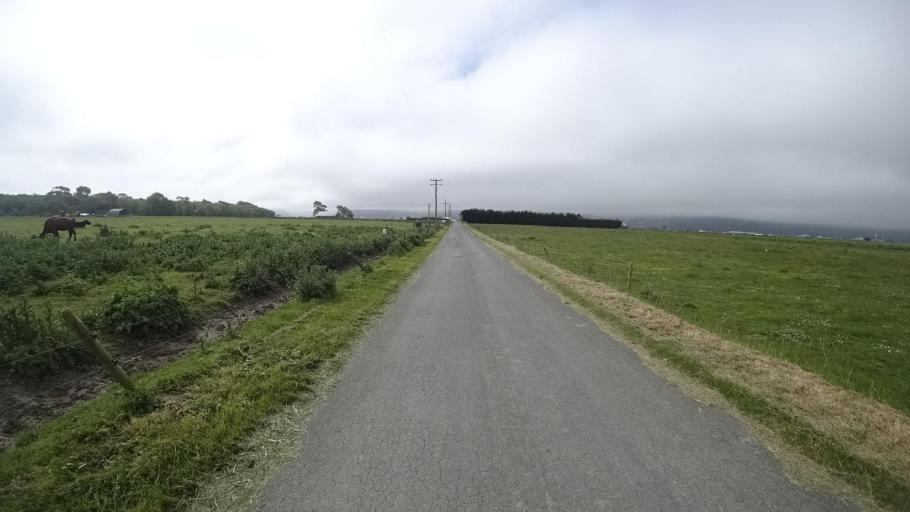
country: US
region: California
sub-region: Humboldt County
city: Fortuna
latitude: 40.5872
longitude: -124.1879
